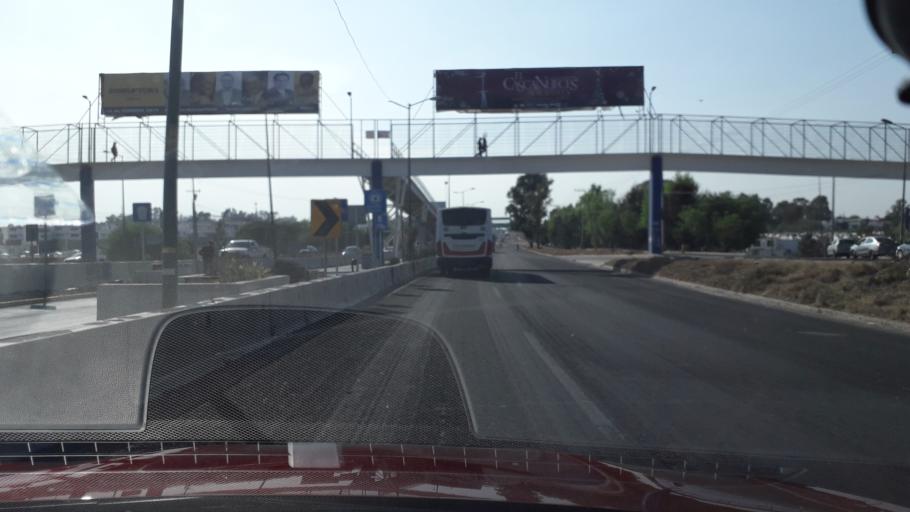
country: MX
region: Puebla
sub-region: Puebla
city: El Capulo (La Quebradora)
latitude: 18.9788
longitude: -98.2202
